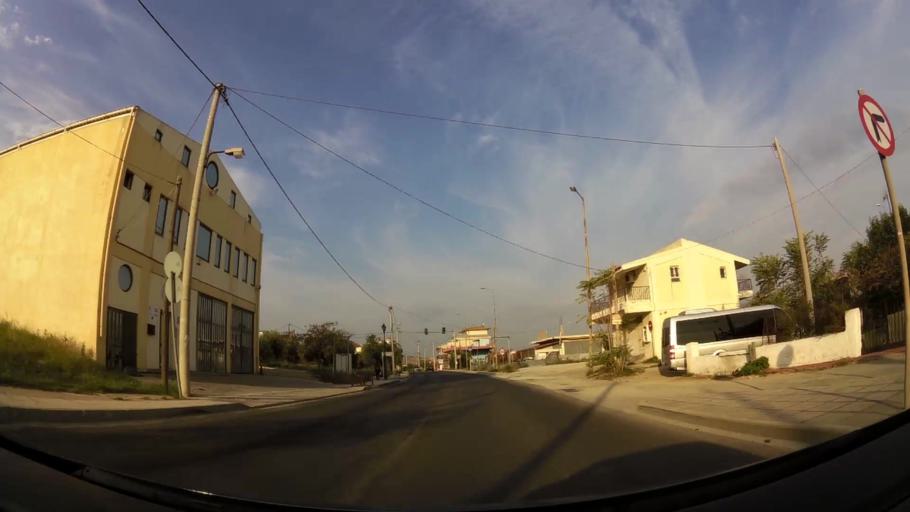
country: GR
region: Attica
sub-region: Nomarchia Dytikis Attikis
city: Ano Liosia
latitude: 38.0711
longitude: 23.6891
